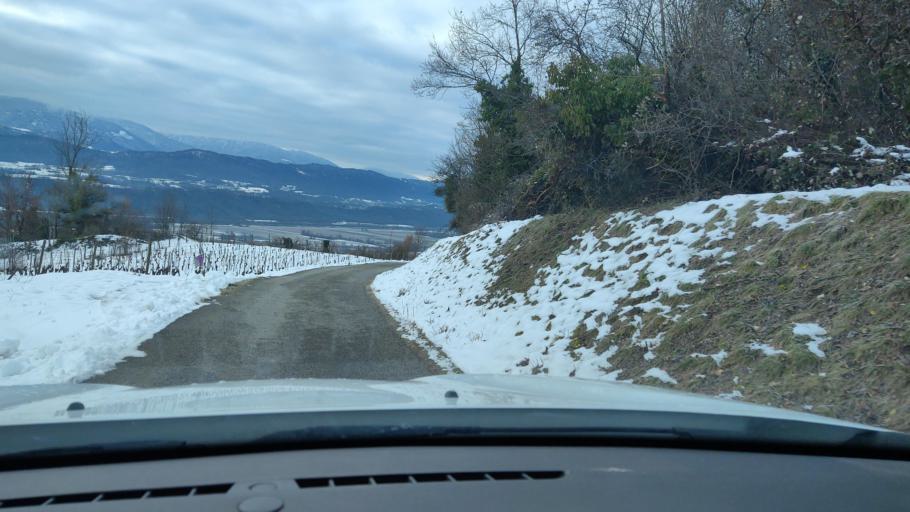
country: FR
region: Rhone-Alpes
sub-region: Departement de la Savoie
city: Coise-Saint-Jean-Pied-Gauthier
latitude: 45.5708
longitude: 6.1373
